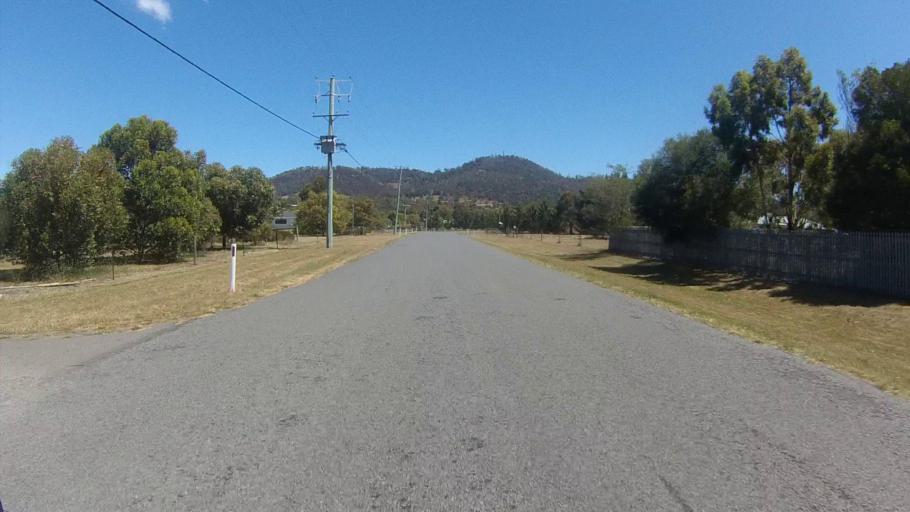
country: AU
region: Tasmania
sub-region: Clarence
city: Cambridge
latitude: -42.8453
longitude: 147.4732
